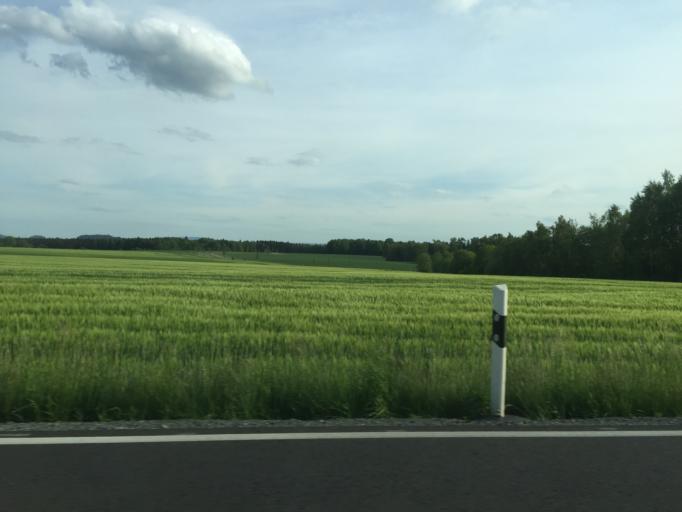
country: DE
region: Saxony
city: Stadt Wehlen
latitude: 50.9879
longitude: 14.0570
